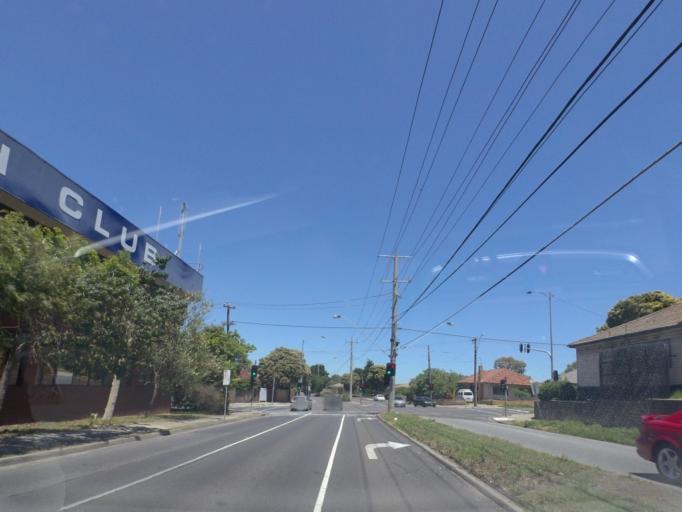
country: AU
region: Victoria
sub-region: Darebin
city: Preston
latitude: -37.7540
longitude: 145.0207
